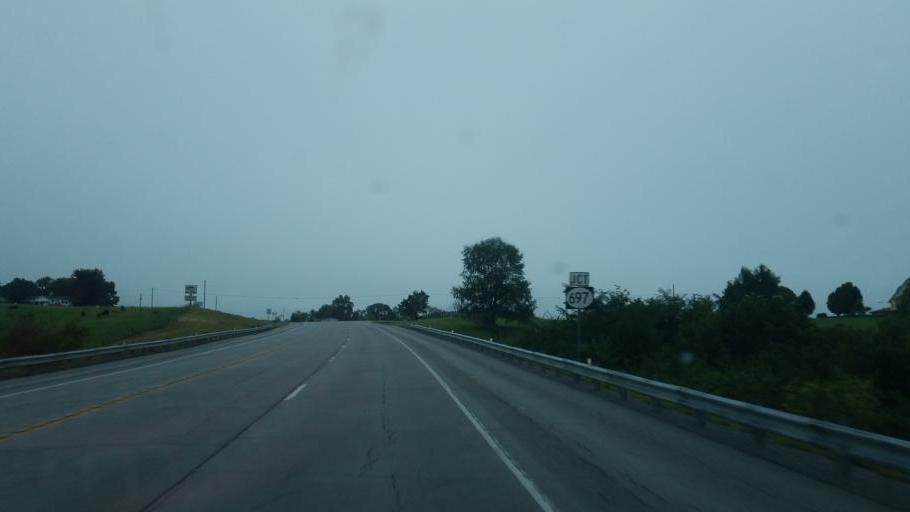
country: US
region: Kentucky
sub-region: Fleming County
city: Flemingsburg
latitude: 38.3955
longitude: -83.7122
